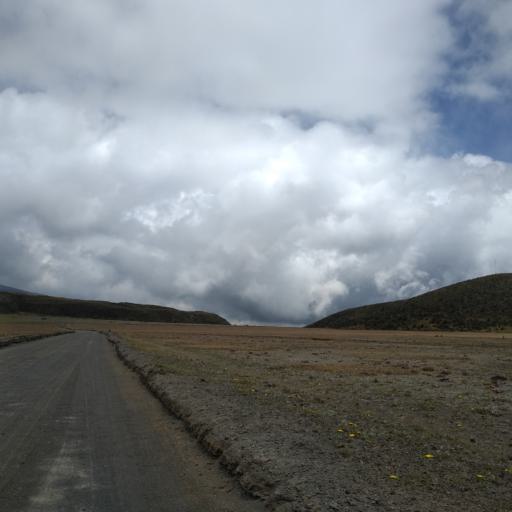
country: EC
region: Pichincha
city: Machachi
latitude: -0.6200
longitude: -78.4744
